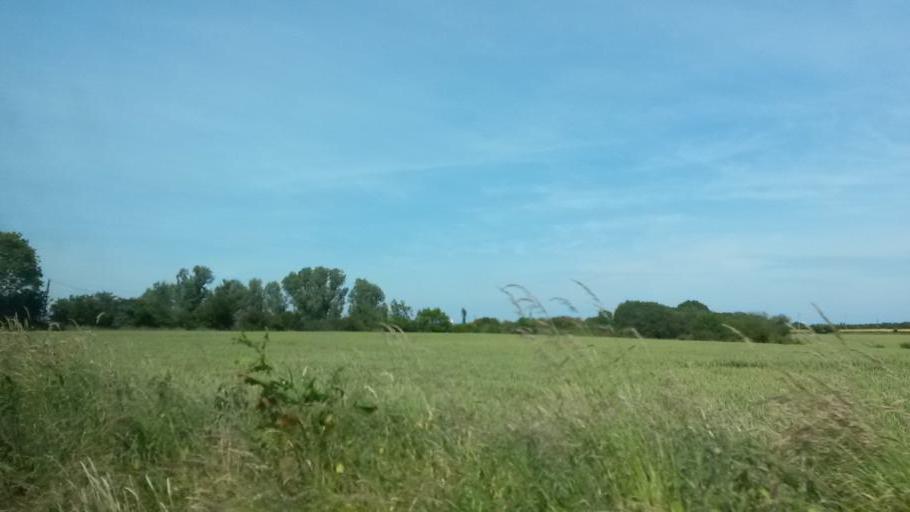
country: IE
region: Leinster
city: Lusk
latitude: 53.5138
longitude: -6.1535
